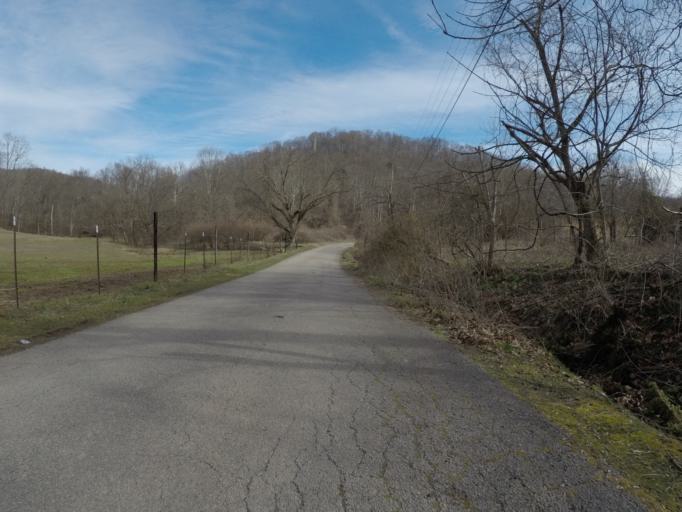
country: US
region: West Virginia
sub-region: Wayne County
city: Lavalette
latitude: 38.3376
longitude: -82.5020
